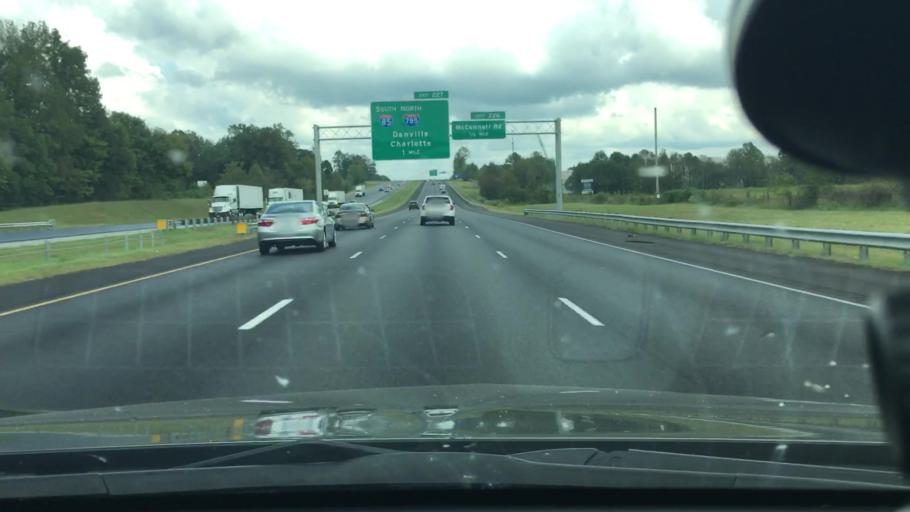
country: US
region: North Carolina
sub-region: Guilford County
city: McLeansville
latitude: 36.0576
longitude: -79.7051
